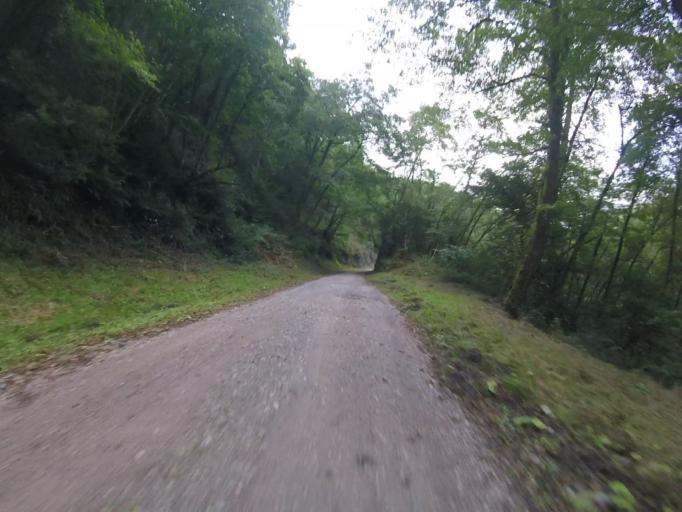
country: ES
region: Basque Country
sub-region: Provincia de Guipuzcoa
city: Elduayen
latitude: 43.1721
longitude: -1.9621
